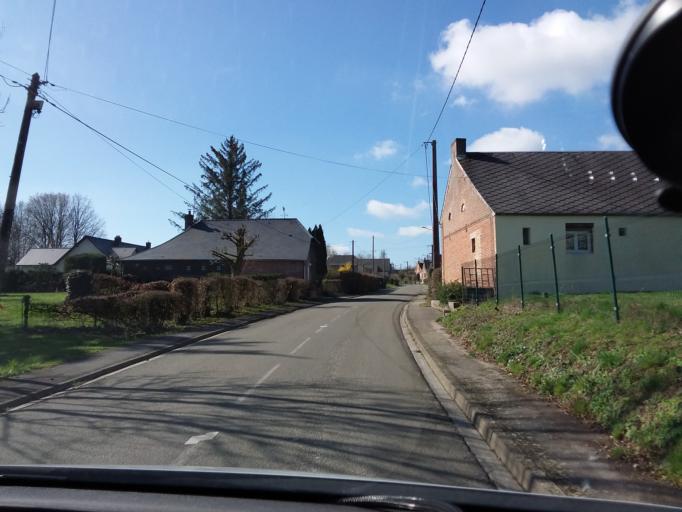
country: FR
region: Picardie
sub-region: Departement de l'Aisne
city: Hirson
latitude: 49.8566
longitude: 4.0878
